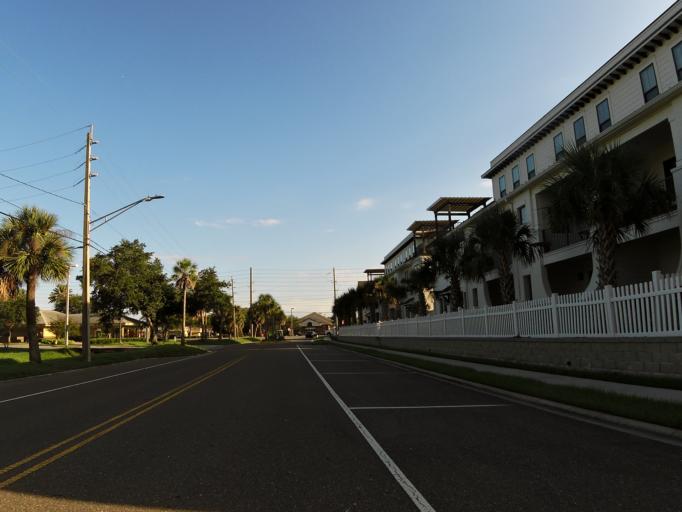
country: US
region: Florida
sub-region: Duval County
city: Atlantic Beach
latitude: 30.3256
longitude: -81.4134
